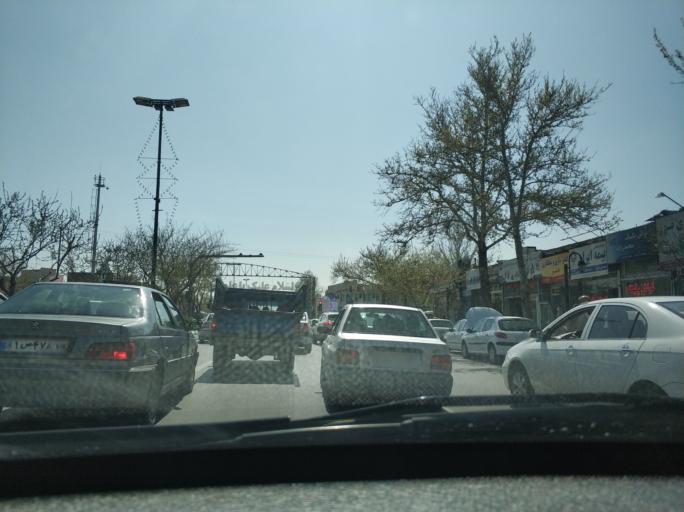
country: IR
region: Razavi Khorasan
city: Mashhad
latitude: 36.2629
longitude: 59.6037
